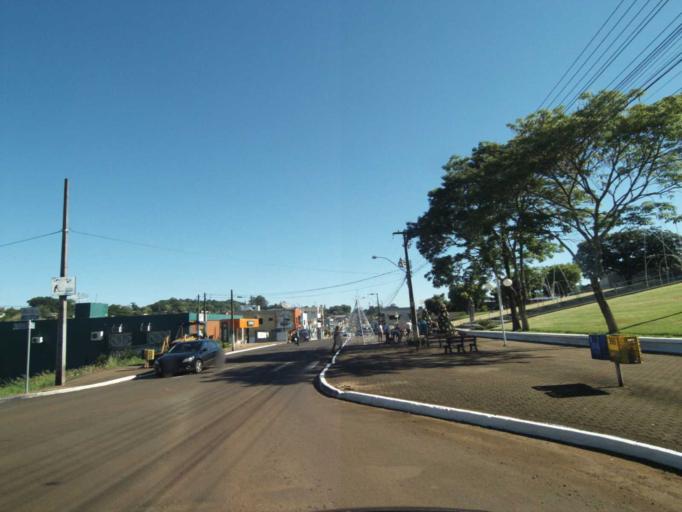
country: BR
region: Parana
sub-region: Coronel Vivida
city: Coronel Vivida
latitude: -25.9648
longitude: -52.8149
